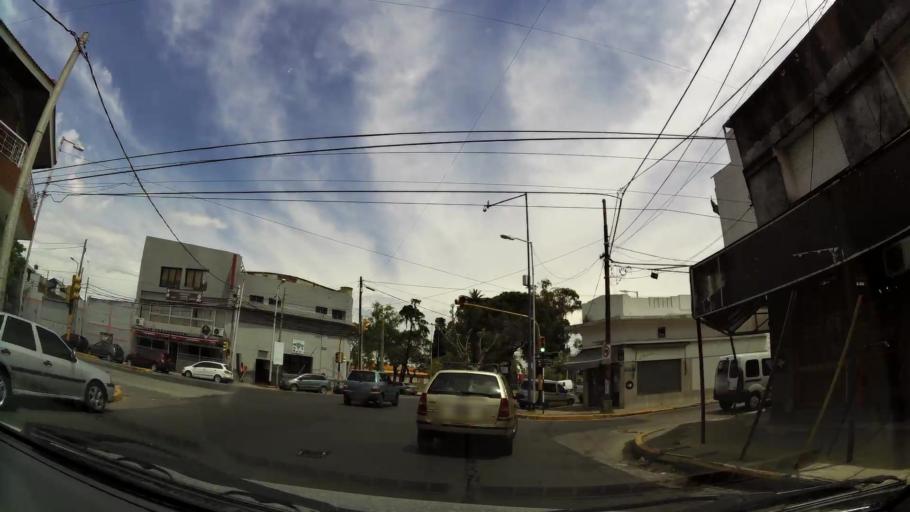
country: AR
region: Buenos Aires
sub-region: Partido de Avellaneda
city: Avellaneda
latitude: -34.6670
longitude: -58.3824
